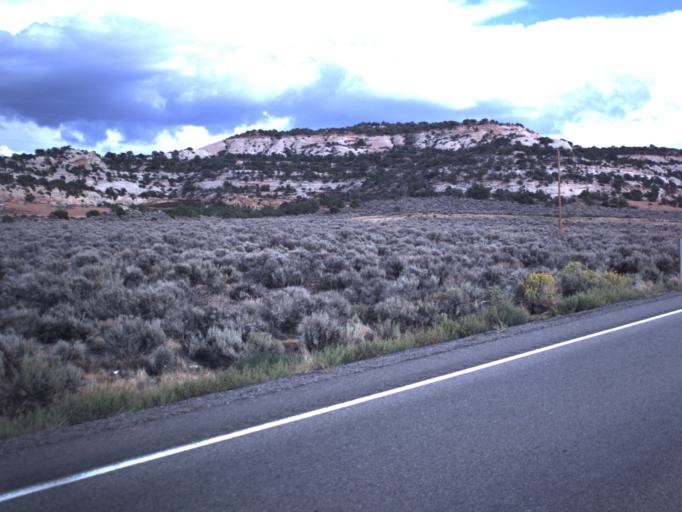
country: US
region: Utah
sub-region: Grand County
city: Moab
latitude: 38.2850
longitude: -109.3739
